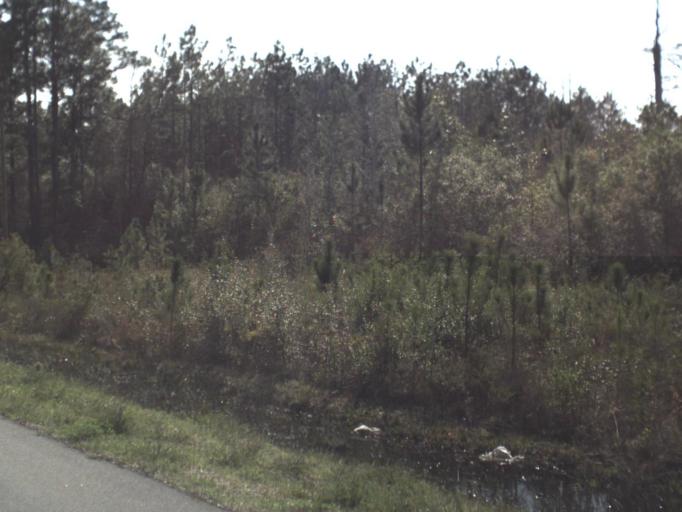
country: US
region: Florida
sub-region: Wakulla County
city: Crawfordville
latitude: 30.0258
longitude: -84.4989
